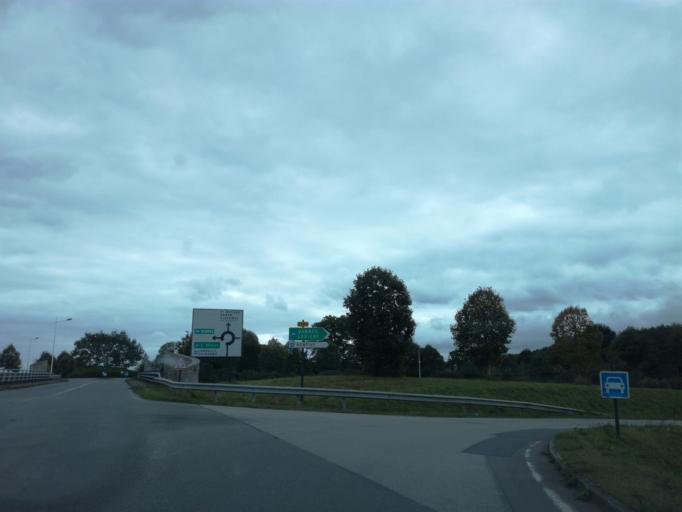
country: FR
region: Brittany
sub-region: Departement des Cotes-d'Armor
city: Loudeac
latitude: 48.1519
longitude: -2.7582
